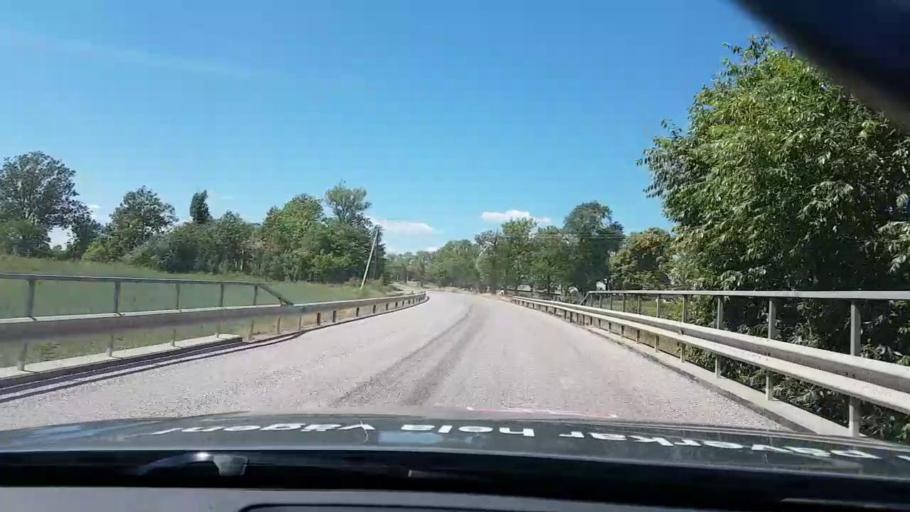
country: SE
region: Kalmar
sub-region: Vasterviks Kommun
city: Forserum
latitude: 57.9409
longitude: 16.4952
